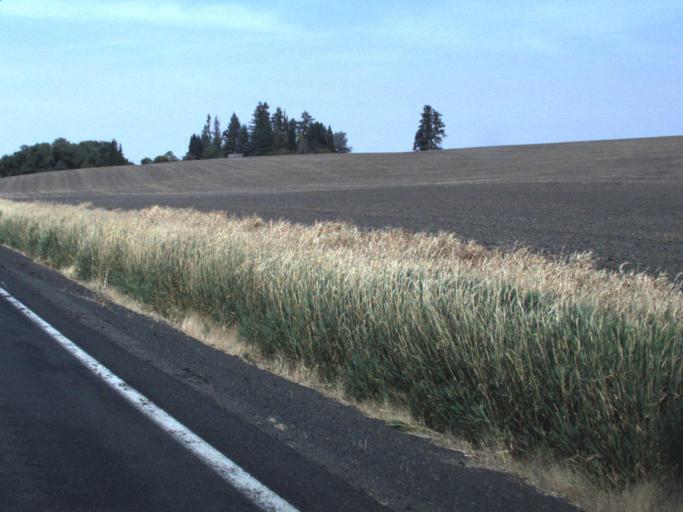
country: US
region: Washington
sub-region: Whitman County
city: Colfax
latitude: 47.1131
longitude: -117.1886
